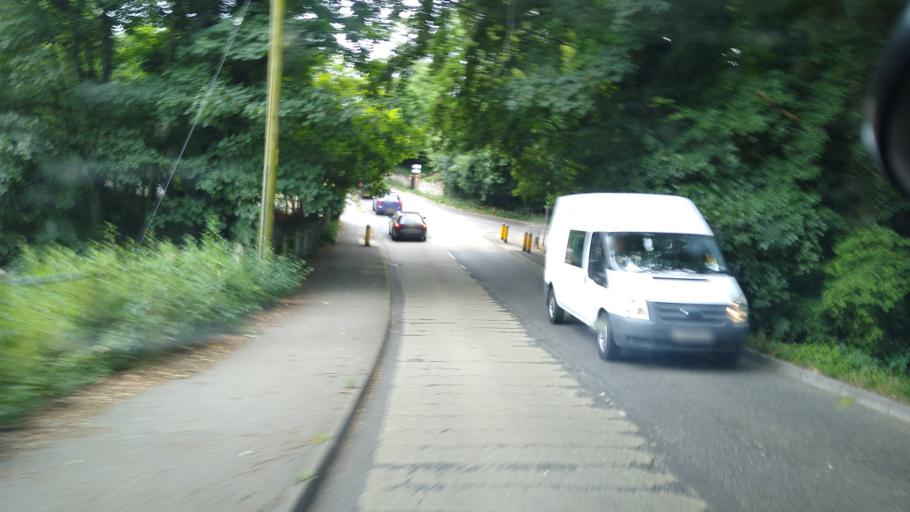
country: GB
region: England
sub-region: Hampshire
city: Alton
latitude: 51.0990
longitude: -0.9450
